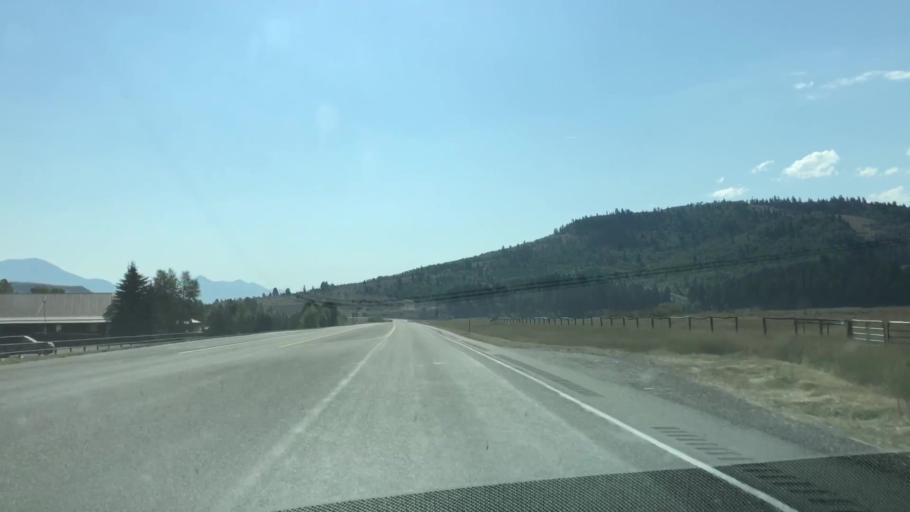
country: US
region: Idaho
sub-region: Teton County
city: Victor
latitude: 43.4616
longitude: -111.4295
